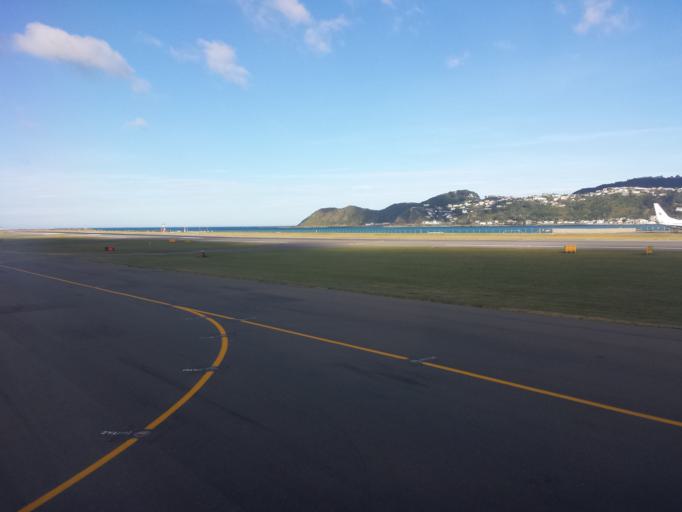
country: NZ
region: Wellington
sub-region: Wellington City
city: Wellington
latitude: -41.3272
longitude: 174.8083
